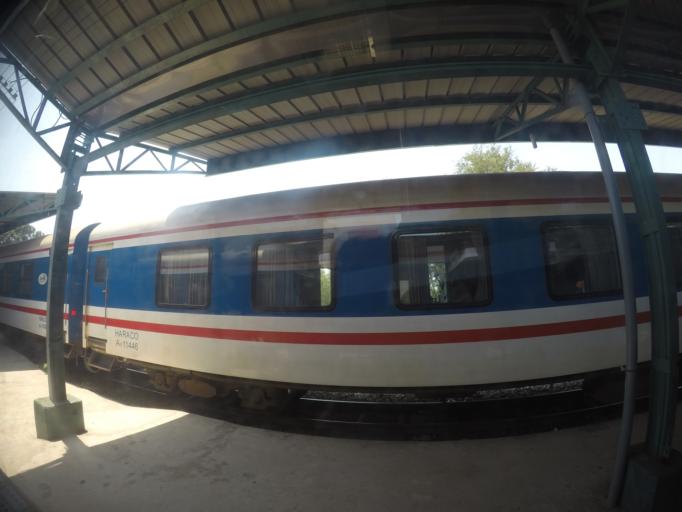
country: VN
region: Binh Thuan
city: Phan Thiet
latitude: 10.9689
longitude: 108.0032
